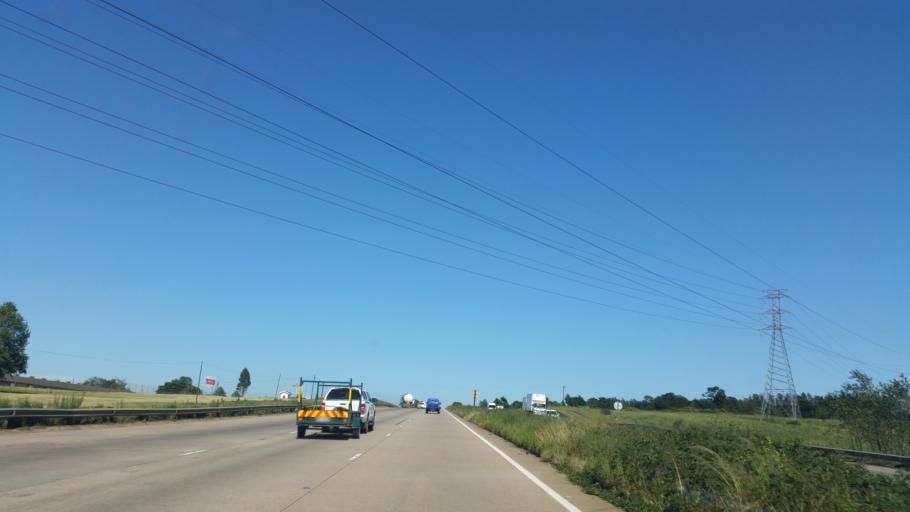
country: ZA
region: KwaZulu-Natal
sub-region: uMgungundlovu District Municipality
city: Camperdown
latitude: -29.7387
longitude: 30.6172
